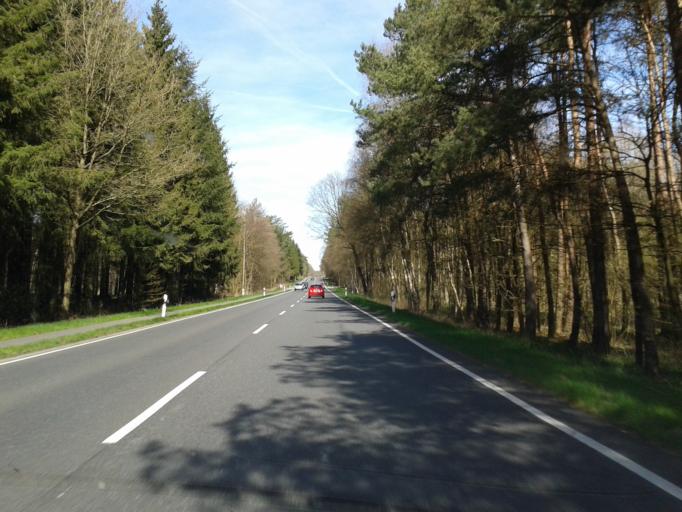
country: DE
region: Lower Saxony
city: Munster
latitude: 52.9596
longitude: 10.1161
